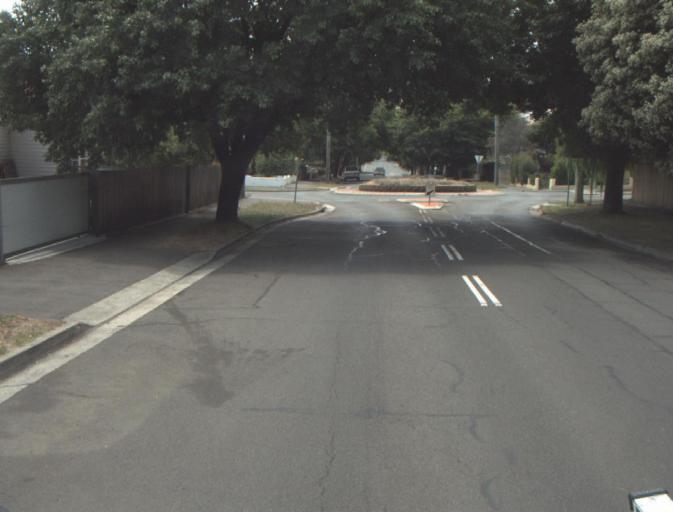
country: AU
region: Tasmania
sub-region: Launceston
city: East Launceston
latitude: -41.4444
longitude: 147.1544
